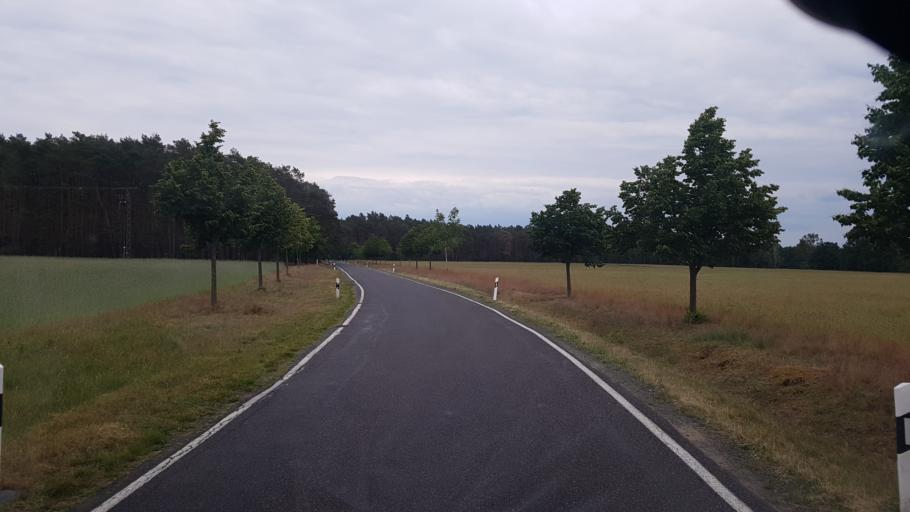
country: DE
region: Brandenburg
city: Herzberg
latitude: 51.7919
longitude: 13.2444
